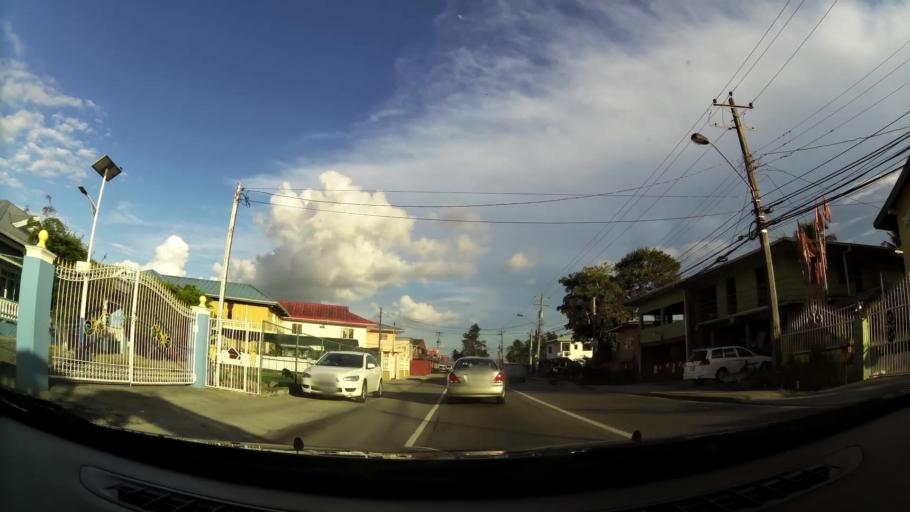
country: TT
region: Tunapuna/Piarco
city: Tunapuna
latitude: 10.5903
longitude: -61.3650
